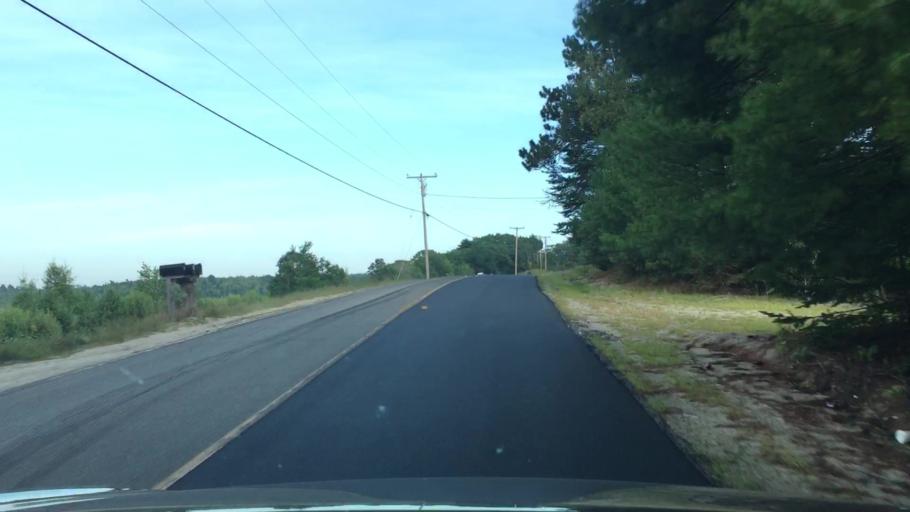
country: US
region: Maine
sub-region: Hancock County
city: Surry
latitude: 44.5156
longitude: -68.6037
